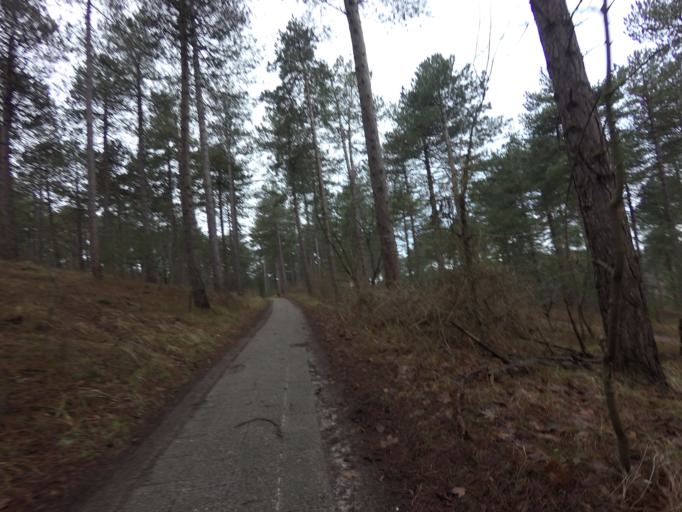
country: NL
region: Zeeland
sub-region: Schouwen-Duiveland
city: Burgh
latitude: 51.6898
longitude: 3.6961
